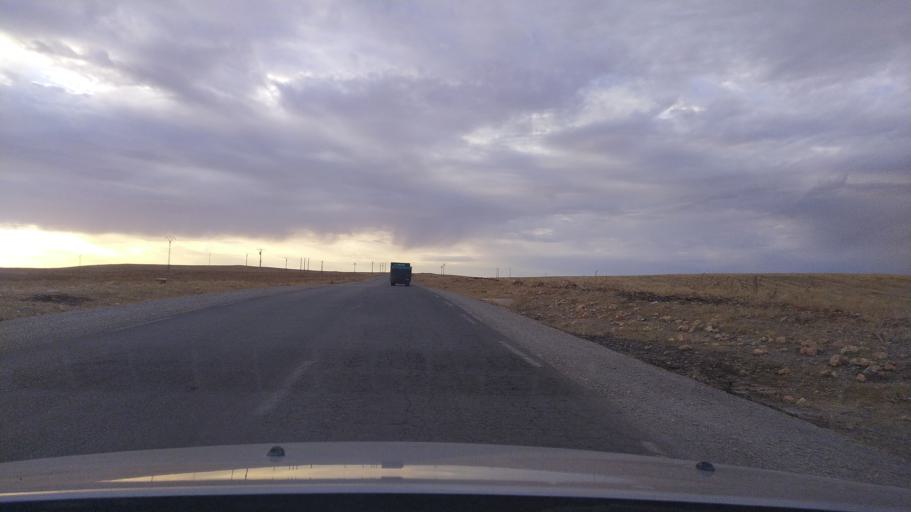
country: DZ
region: Tiaret
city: Frenda
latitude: 34.9865
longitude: 1.1366
